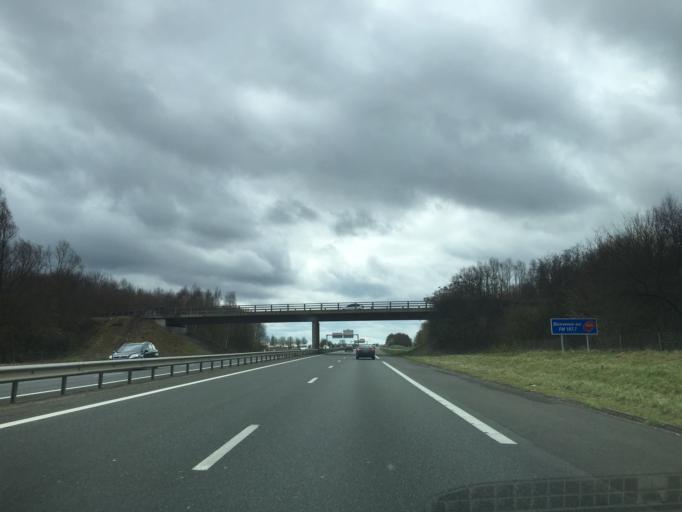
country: FR
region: Ile-de-France
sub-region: Departement de Seine-et-Marne
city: Moissy-Cramayel
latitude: 48.6147
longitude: 2.6315
